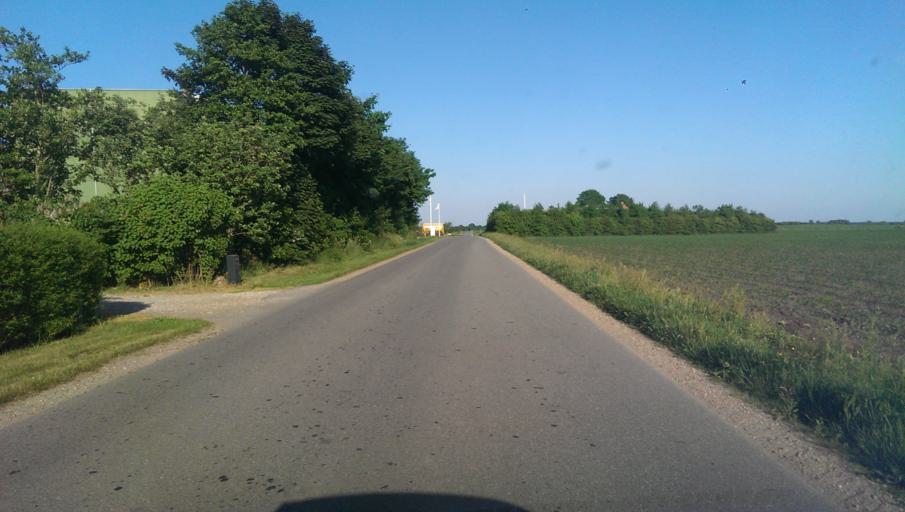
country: DK
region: South Denmark
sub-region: Esbjerg Kommune
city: Bramming
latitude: 55.5482
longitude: 8.6529
